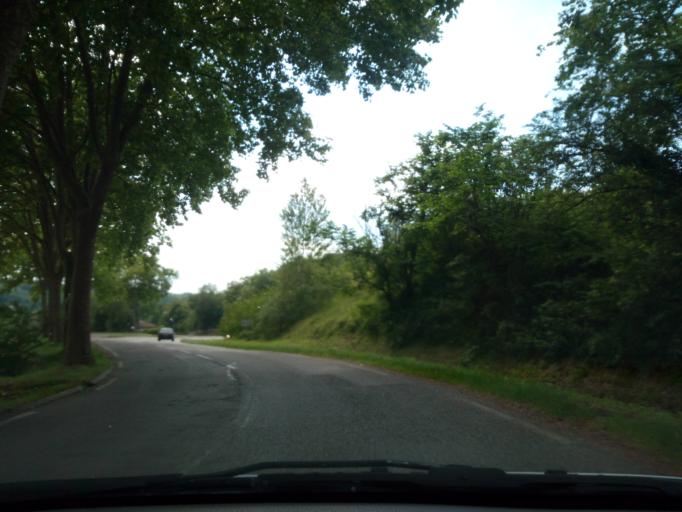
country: FR
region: Midi-Pyrenees
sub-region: Departement du Tarn-et-Garonne
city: Lafrancaise
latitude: 44.1279
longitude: 1.2375
